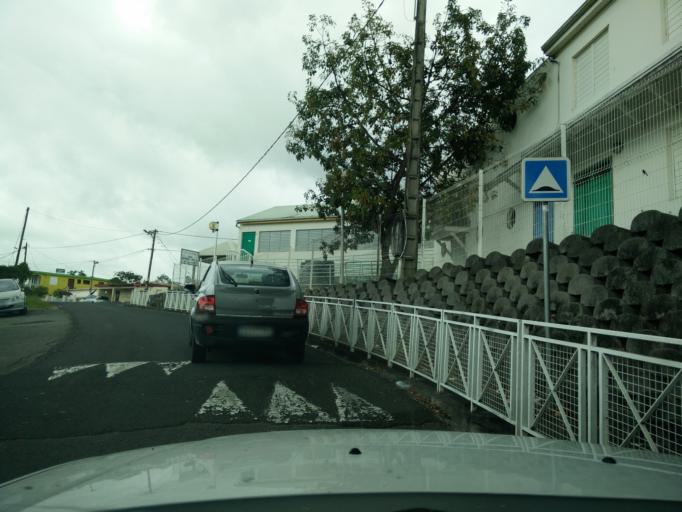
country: GP
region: Guadeloupe
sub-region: Guadeloupe
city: Le Gosier
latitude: 16.2302
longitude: -61.4586
